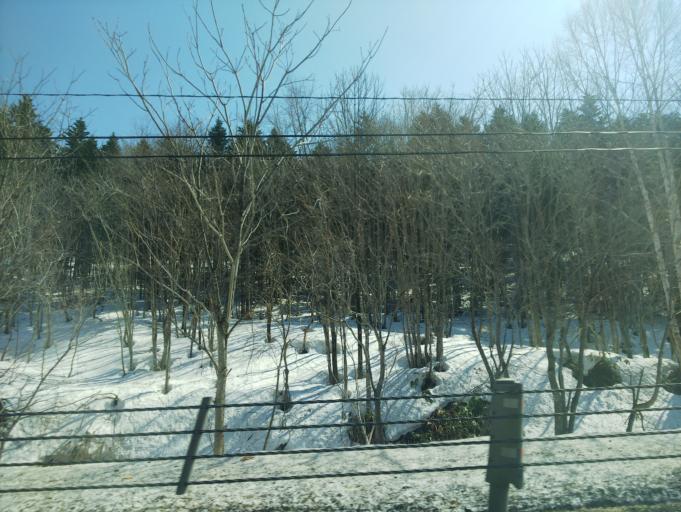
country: JP
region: Hokkaido
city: Nayoro
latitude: 44.7097
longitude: 142.2750
